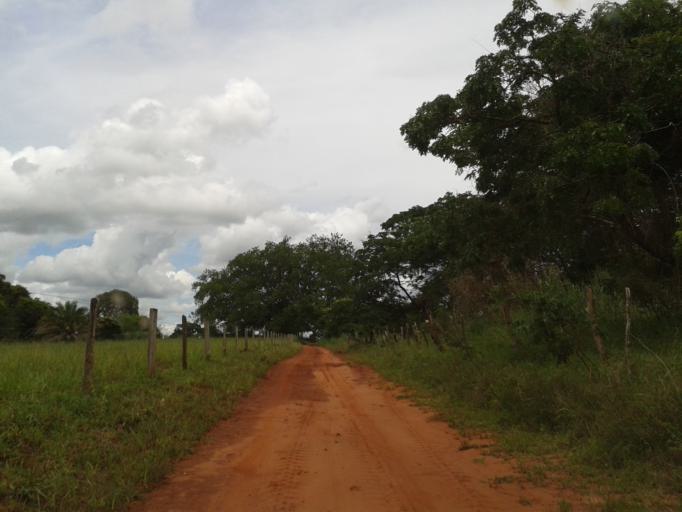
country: BR
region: Minas Gerais
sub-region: Santa Vitoria
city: Santa Vitoria
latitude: -18.7929
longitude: -49.8520
